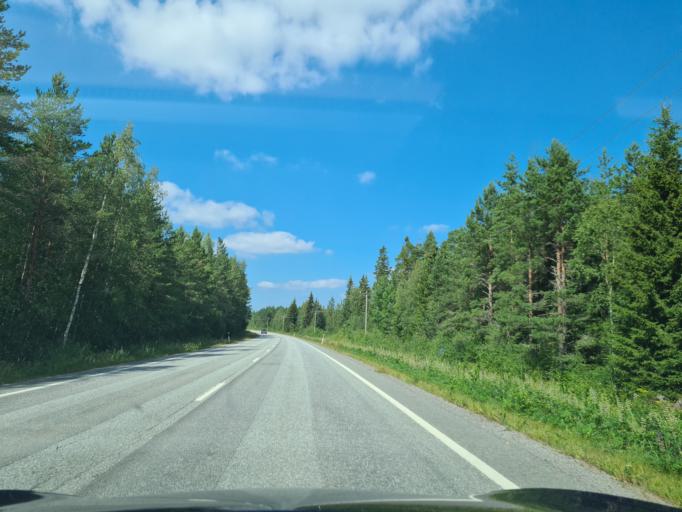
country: FI
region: Ostrobothnia
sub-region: Vaasa
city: Vaasa
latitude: 63.1774
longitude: 21.5763
